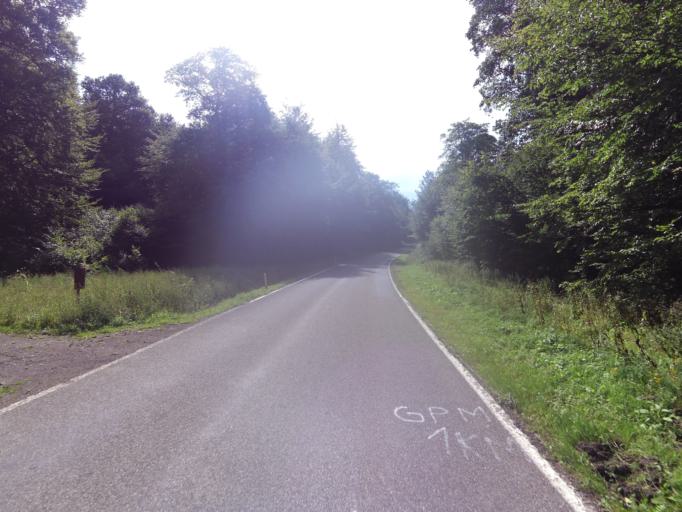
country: BE
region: Wallonia
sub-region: Province du Luxembourg
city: Saint-Hubert
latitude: 50.0657
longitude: 5.3462
